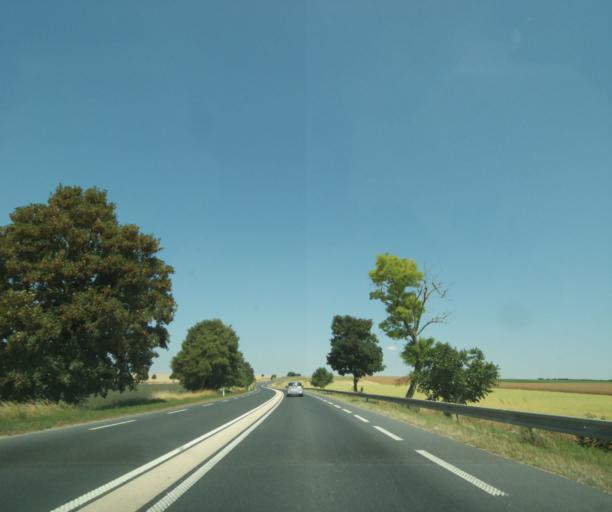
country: FR
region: Champagne-Ardenne
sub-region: Departement de la Marne
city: Mourmelon-le-Grand
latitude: 49.0699
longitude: 4.2940
